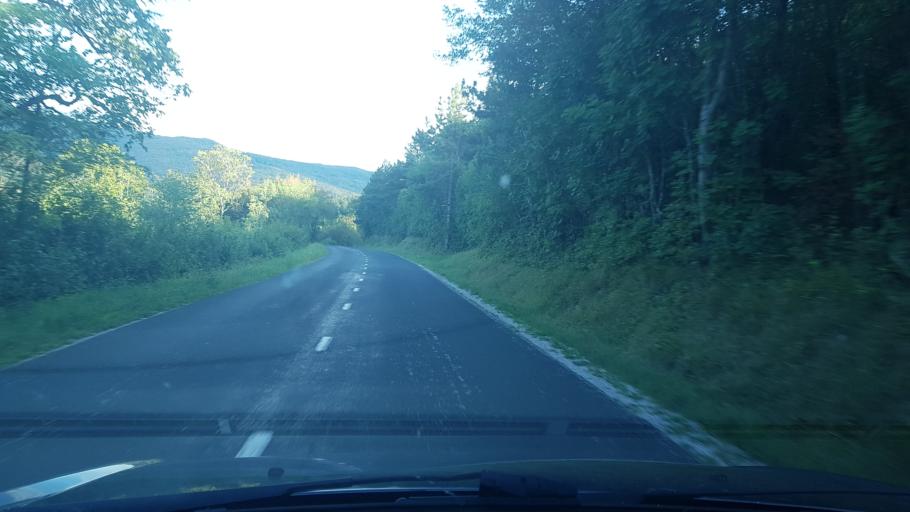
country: SI
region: Nova Gorica
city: Solkan
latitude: 46.0189
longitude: 13.6795
